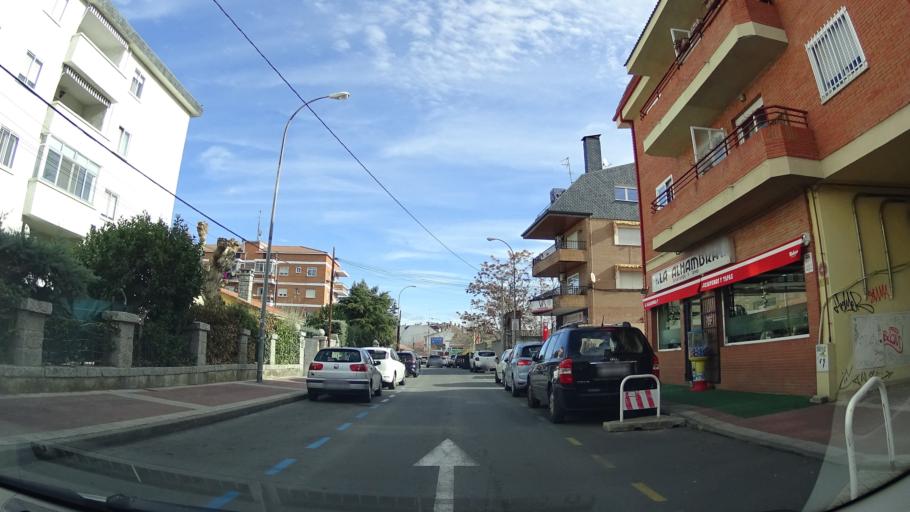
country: ES
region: Madrid
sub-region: Provincia de Madrid
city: Collado-Villalba
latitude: 40.6274
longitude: -4.0114
